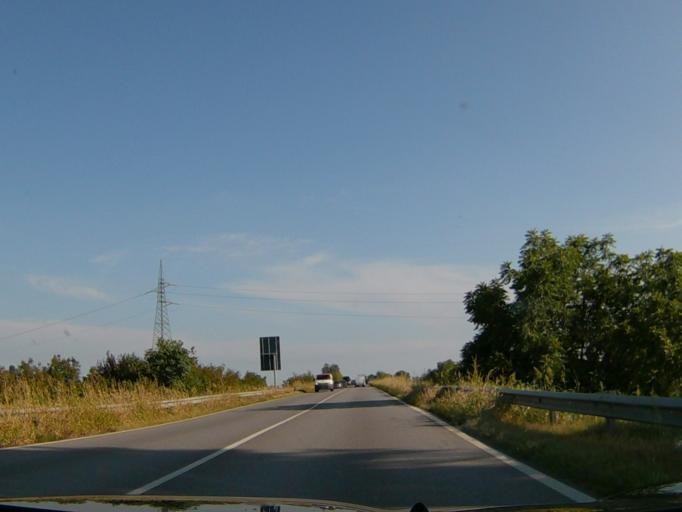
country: IT
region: Lombardy
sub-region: Provincia di Brescia
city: Travagliato
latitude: 45.5098
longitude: 10.0687
